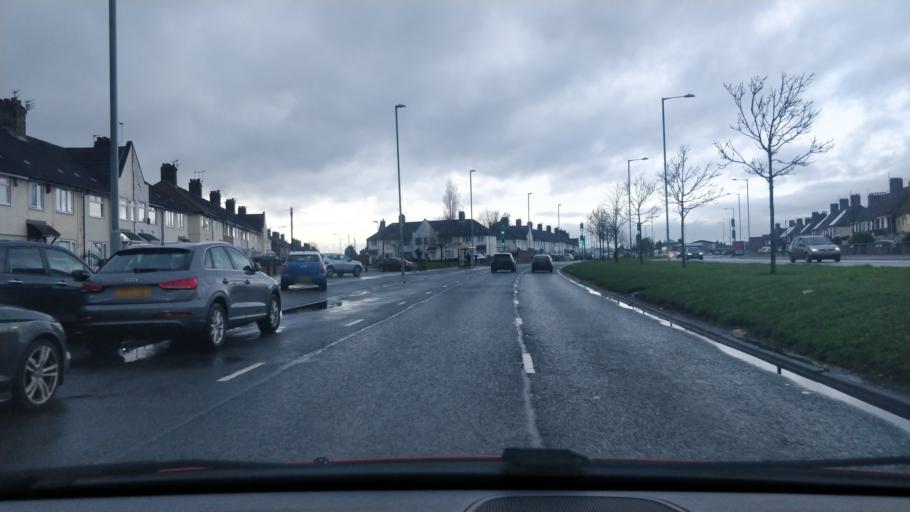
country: GB
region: England
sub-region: Knowsley
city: Huyton
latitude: 53.4204
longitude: -2.8542
